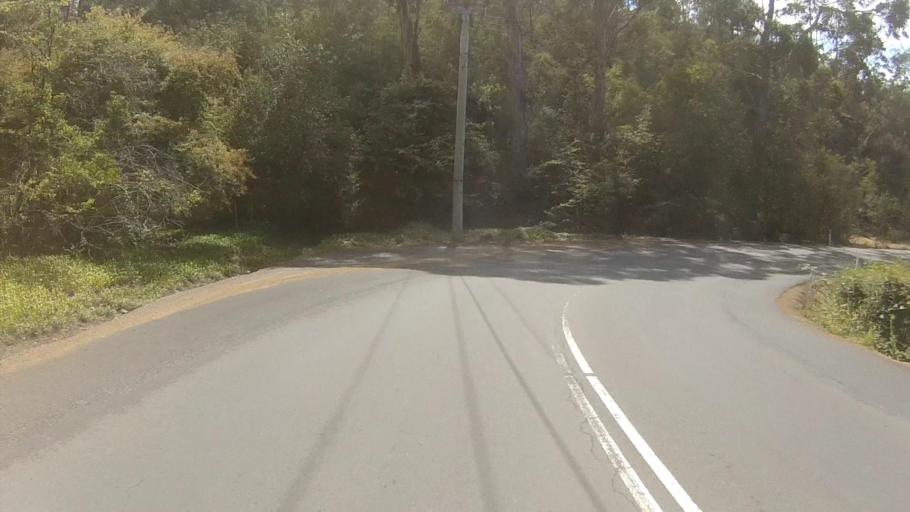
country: AU
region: Tasmania
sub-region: Kingborough
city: Taroona
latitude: -42.9567
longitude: 147.3388
